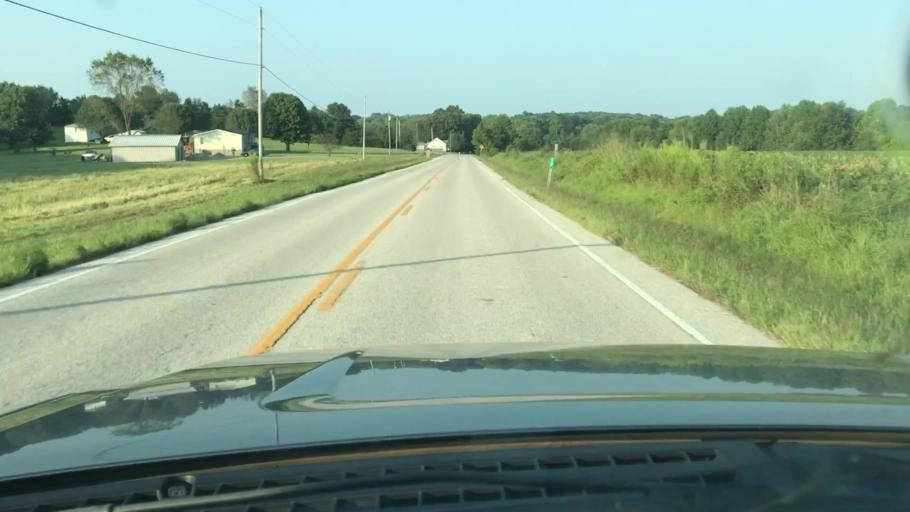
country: US
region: Tennessee
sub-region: Sumner County
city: Westmoreland
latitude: 36.5745
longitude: -86.3761
